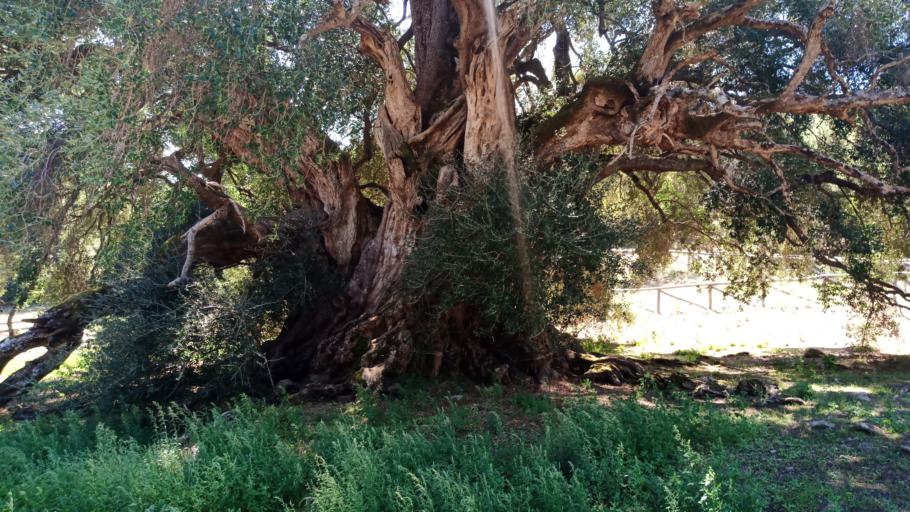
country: IT
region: Sardinia
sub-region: Provincia di Olbia-Tempio
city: Sant'Antonio di Gallura
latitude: 41.0068
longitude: 9.2549
